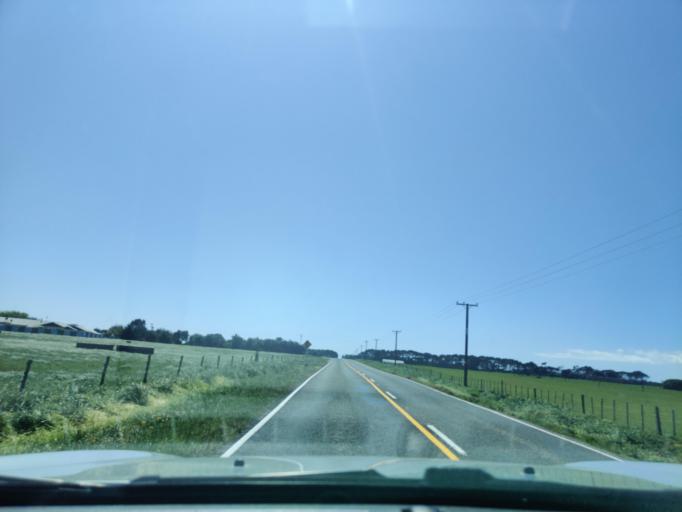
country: NZ
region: Taranaki
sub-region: South Taranaki District
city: Opunake
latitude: -39.3751
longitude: 173.8093
